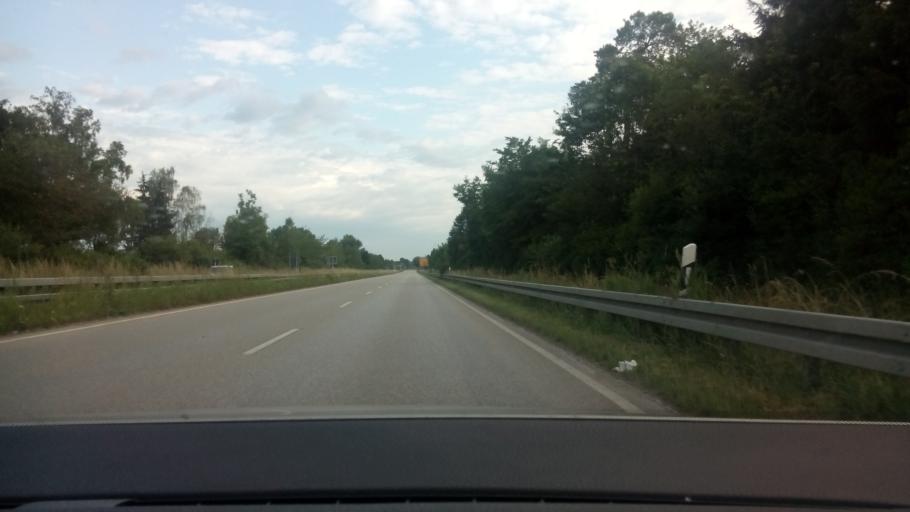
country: DE
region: Bavaria
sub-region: Upper Bavaria
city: Unterschleissheim
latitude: 48.2661
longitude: 11.5946
